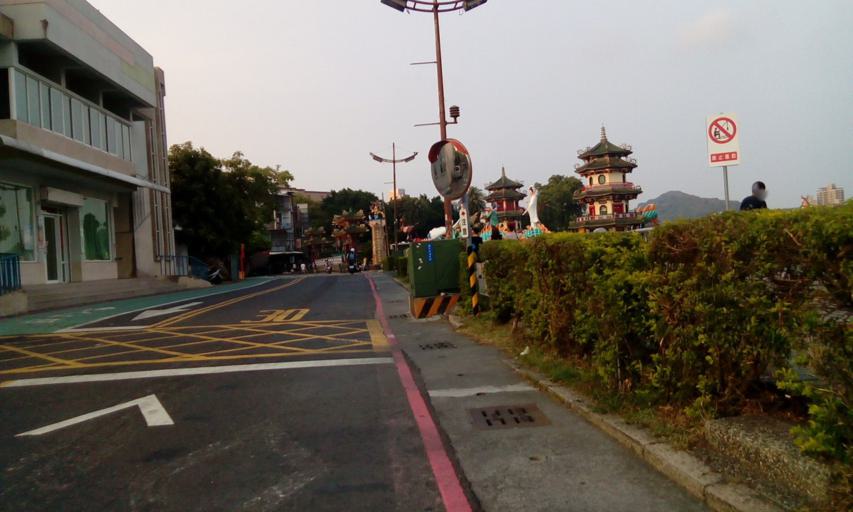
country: TW
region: Kaohsiung
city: Kaohsiung
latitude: 22.6814
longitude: 120.2922
